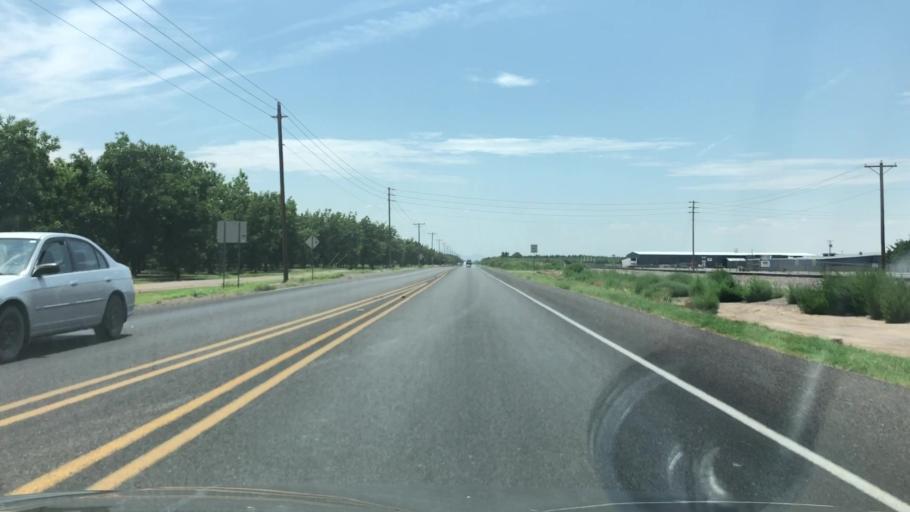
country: US
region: New Mexico
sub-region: Dona Ana County
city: University Park
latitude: 32.2377
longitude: -106.7428
